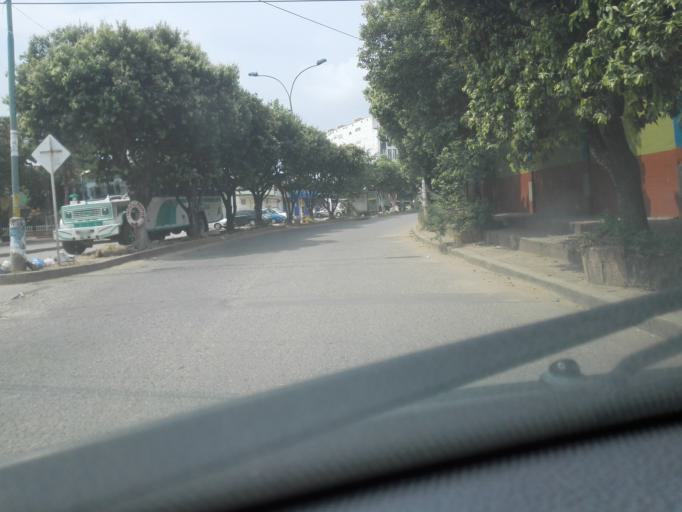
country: CO
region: Santander
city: Floridablanca
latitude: 7.0807
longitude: -73.1235
